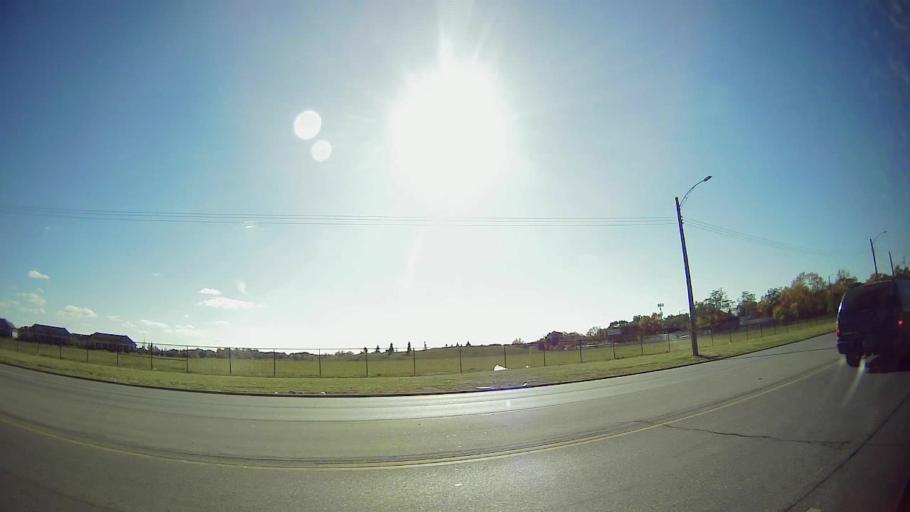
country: US
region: Michigan
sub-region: Wayne County
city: Dearborn
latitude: 42.3579
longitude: -83.2148
